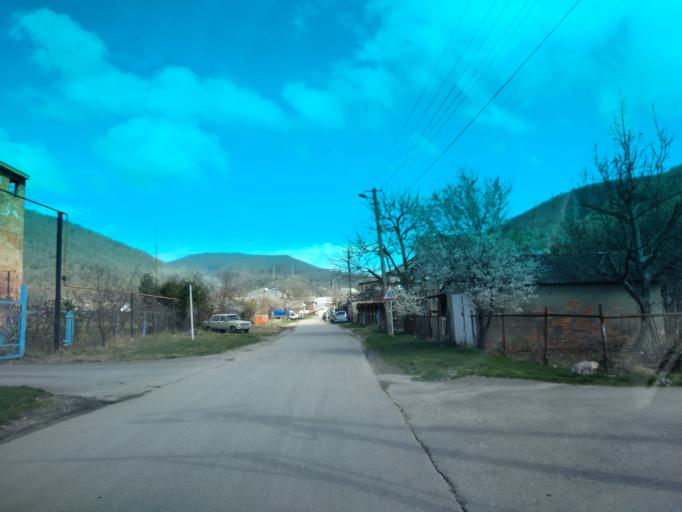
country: RU
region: Krasnodarskiy
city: Shepsi
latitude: 44.0507
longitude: 39.1608
